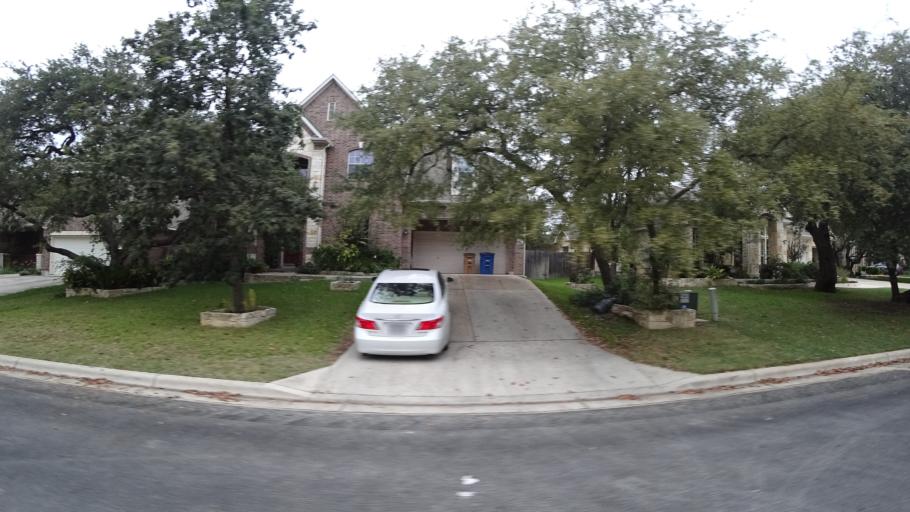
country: US
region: Texas
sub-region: Travis County
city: Shady Hollow
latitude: 30.1872
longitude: -97.9084
